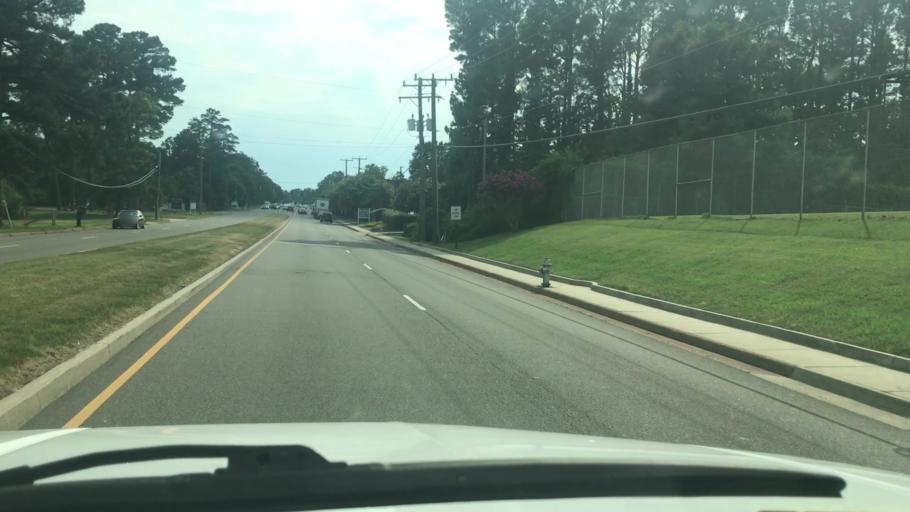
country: US
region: Virginia
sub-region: Henrico County
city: Tuckahoe
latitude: 37.6274
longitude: -77.5479
